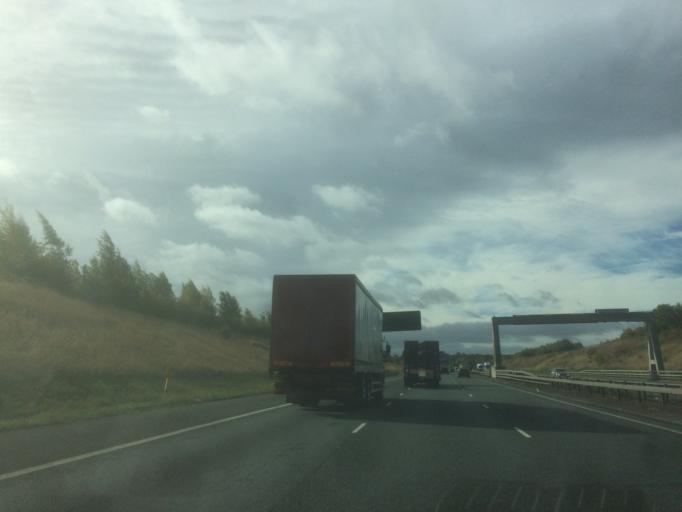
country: GB
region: England
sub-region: North Yorkshire
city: Byram
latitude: 53.7389
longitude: -1.2786
